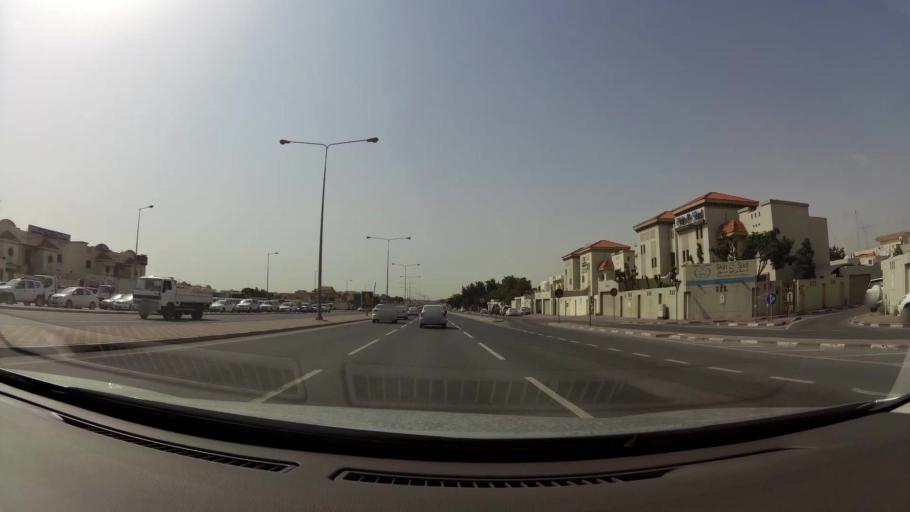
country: QA
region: Baladiyat ad Dawhah
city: Doha
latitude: 25.2531
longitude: 51.5242
